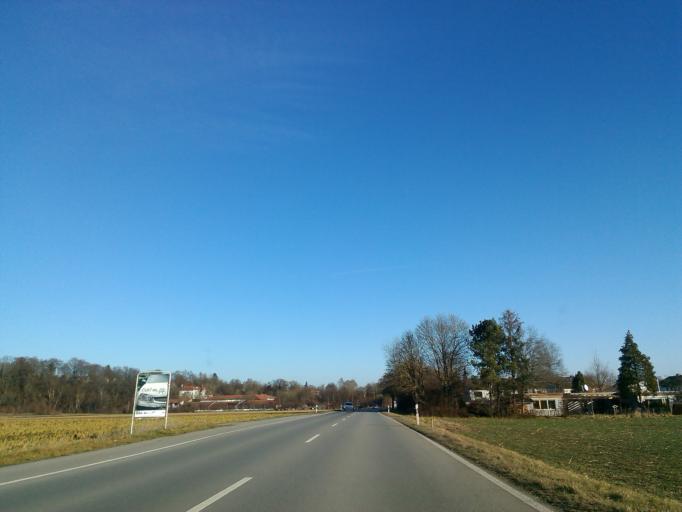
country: DE
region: Bavaria
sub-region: Upper Bavaria
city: Gauting
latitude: 48.0595
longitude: 11.3723
